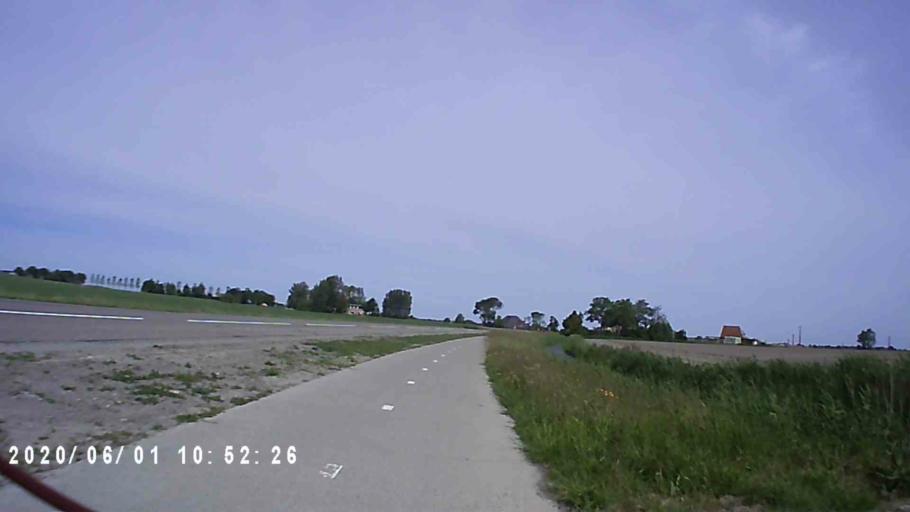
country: NL
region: Friesland
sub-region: Gemeente Franekeradeel
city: Franeker
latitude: 53.1998
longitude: 5.5181
